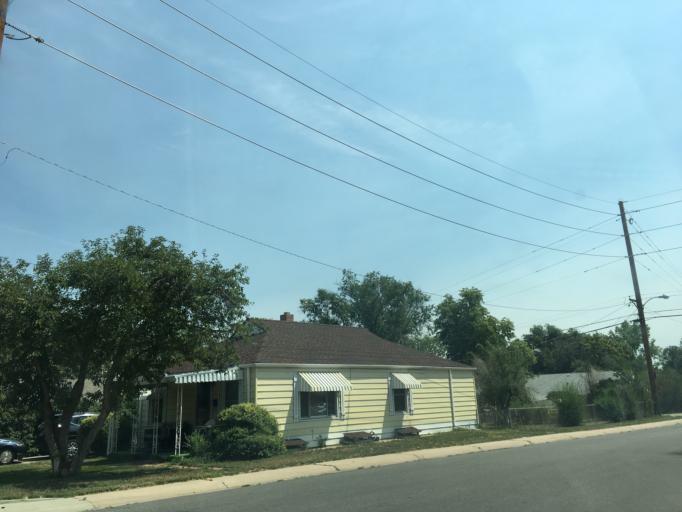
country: US
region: Colorado
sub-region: Jefferson County
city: Lakewood
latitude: 39.6984
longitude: -105.0425
